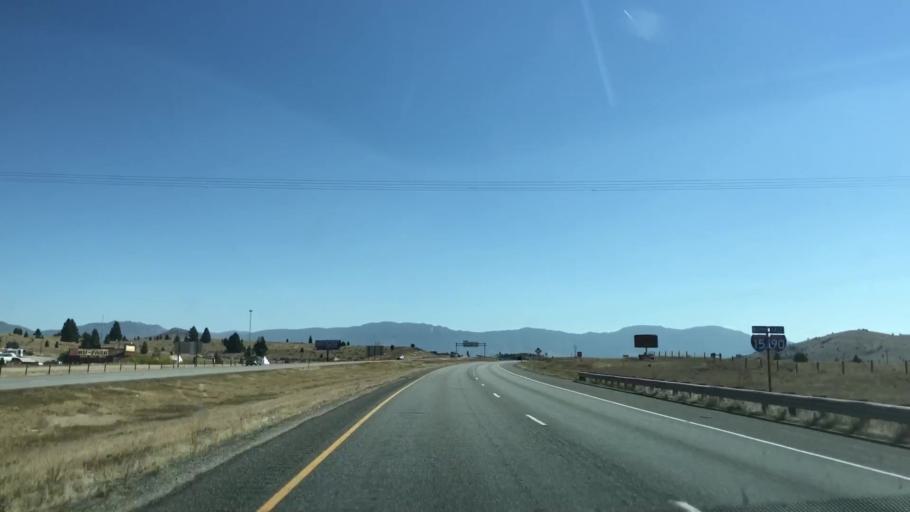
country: US
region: Montana
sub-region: Silver Bow County
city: Butte
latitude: 46.0079
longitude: -112.6278
